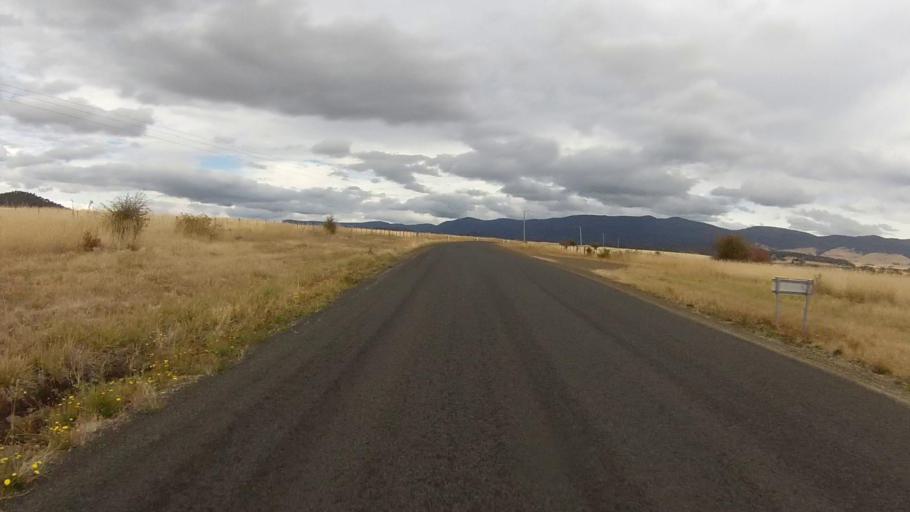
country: AU
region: Tasmania
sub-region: Northern Midlands
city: Evandale
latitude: -41.8189
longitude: 147.7552
